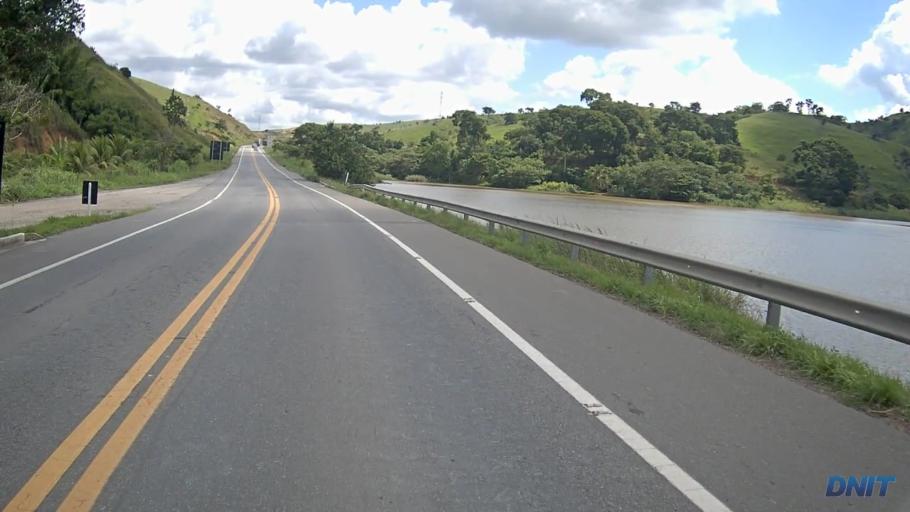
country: BR
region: Minas Gerais
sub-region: Governador Valadares
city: Governador Valadares
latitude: -19.0375
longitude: -42.1480
